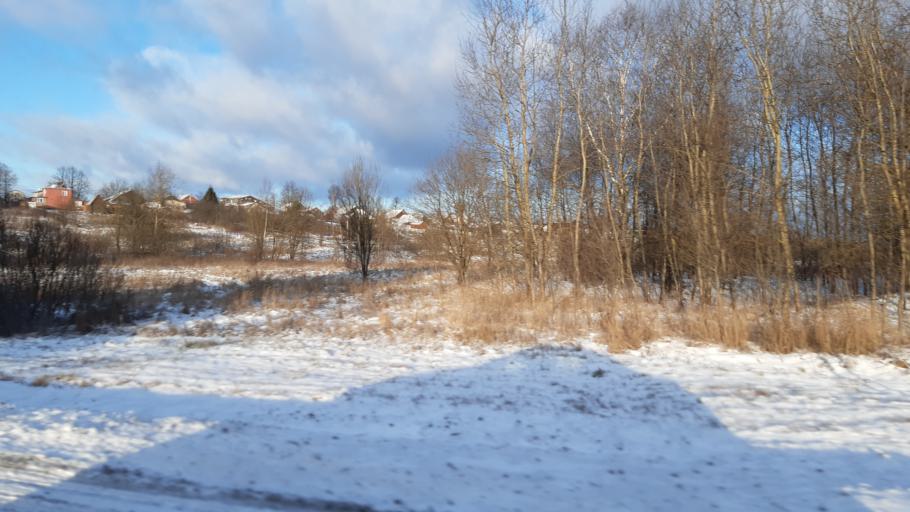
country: RU
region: Moskovskaya
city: Svatkovo
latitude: 56.3093
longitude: 38.3230
